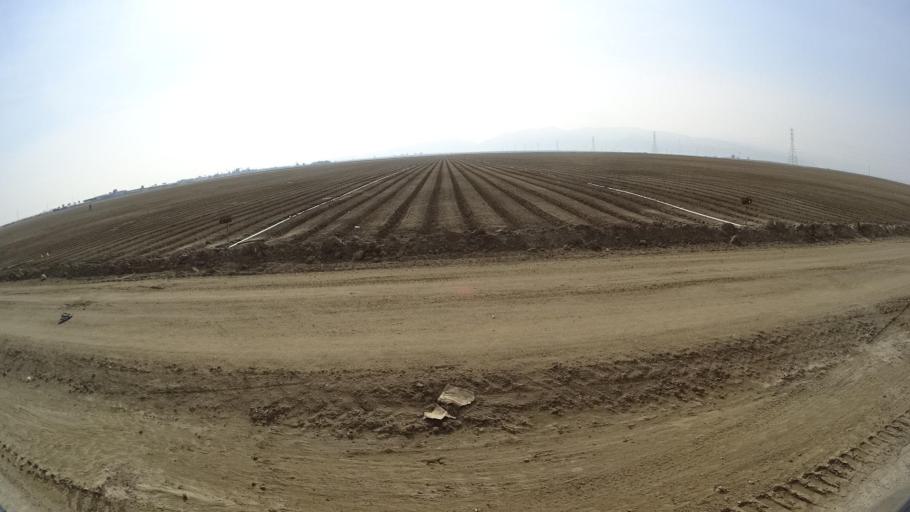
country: US
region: California
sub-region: Kern County
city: Weedpatch
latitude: 35.0762
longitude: -118.9801
